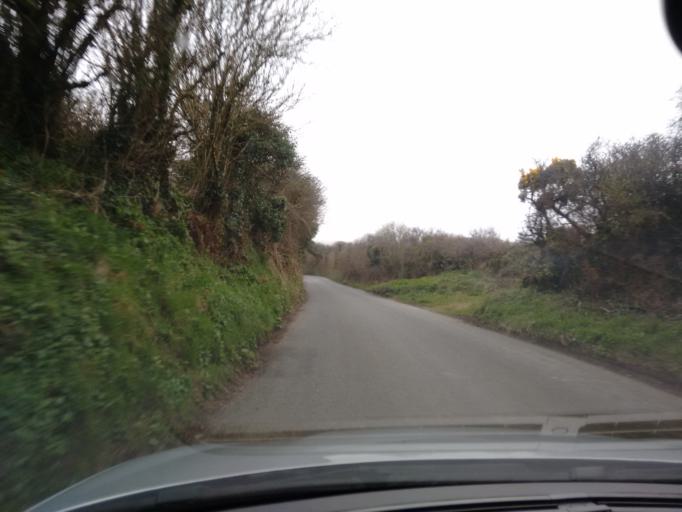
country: GB
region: England
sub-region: Cornwall
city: Tintagel
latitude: 50.6627
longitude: -4.7258
